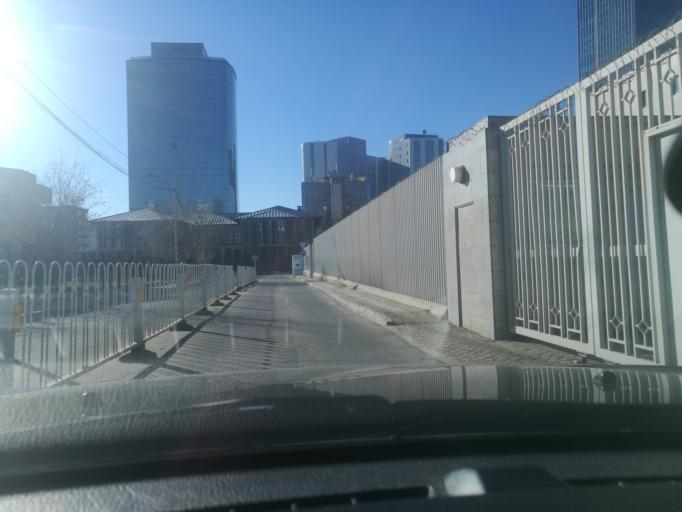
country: MN
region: Ulaanbaatar
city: Ulaanbaatar
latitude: 47.9150
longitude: 106.9236
